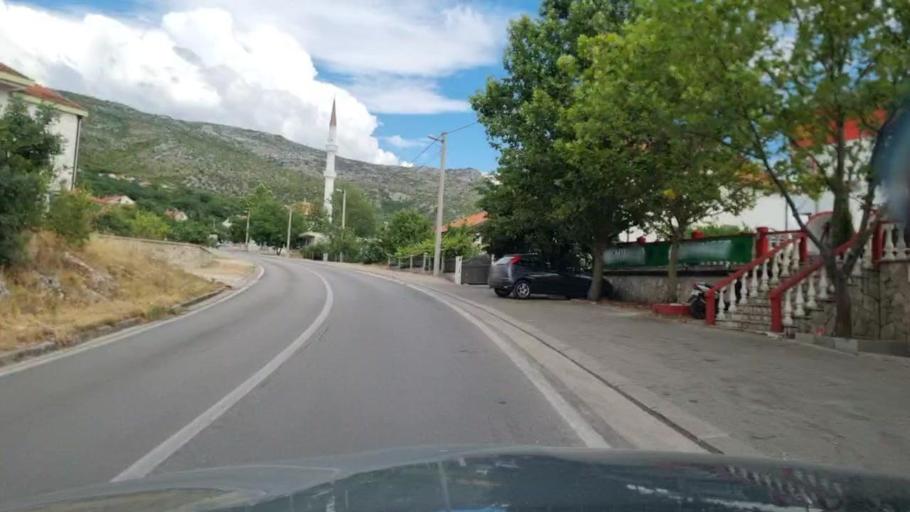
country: BA
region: Federation of Bosnia and Herzegovina
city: Blagaj
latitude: 43.2803
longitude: 17.8707
